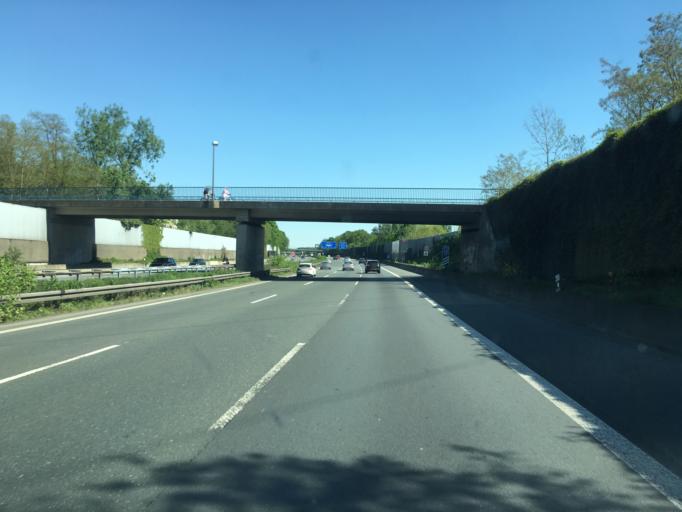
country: DE
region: North Rhine-Westphalia
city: Castrop-Rauxel
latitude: 51.5906
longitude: 7.3491
